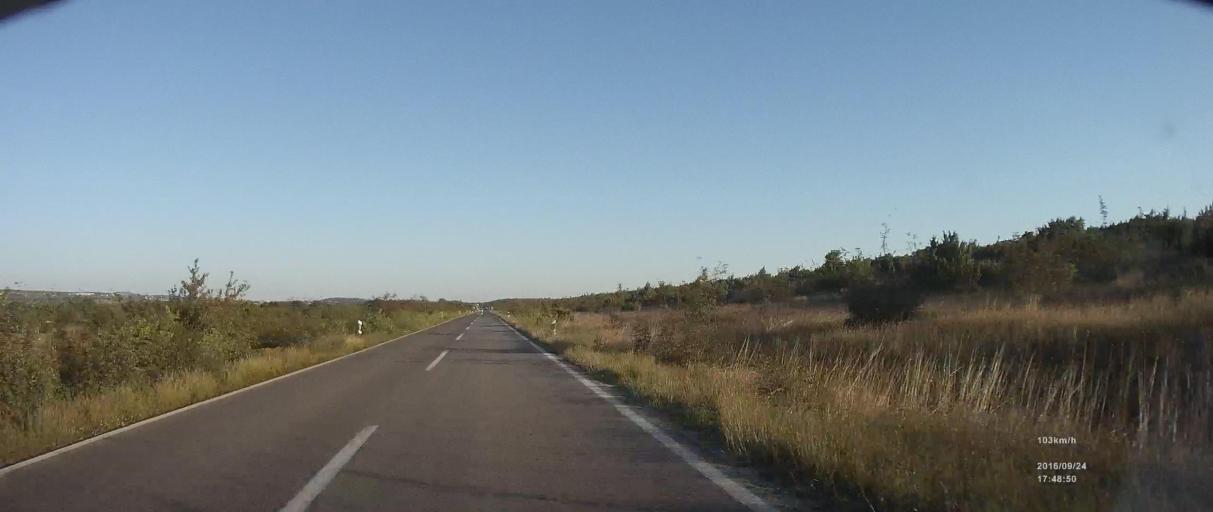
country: HR
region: Zadarska
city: Polaca
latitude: 44.0605
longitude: 15.5417
